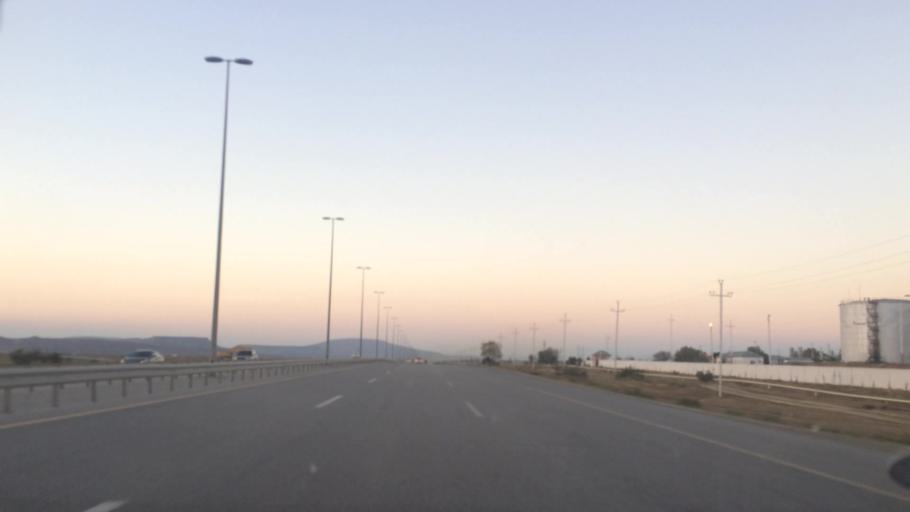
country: AZ
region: Baki
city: Qobustan
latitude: 39.9989
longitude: 49.4306
